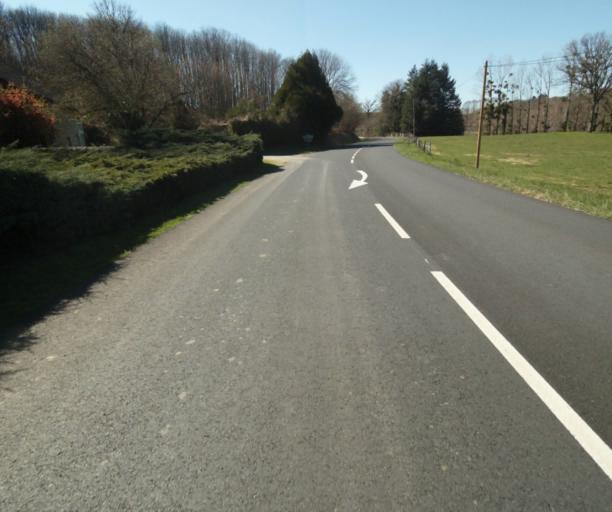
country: FR
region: Limousin
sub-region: Departement de la Correze
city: Saint-Mexant
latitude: 45.2794
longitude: 1.6574
